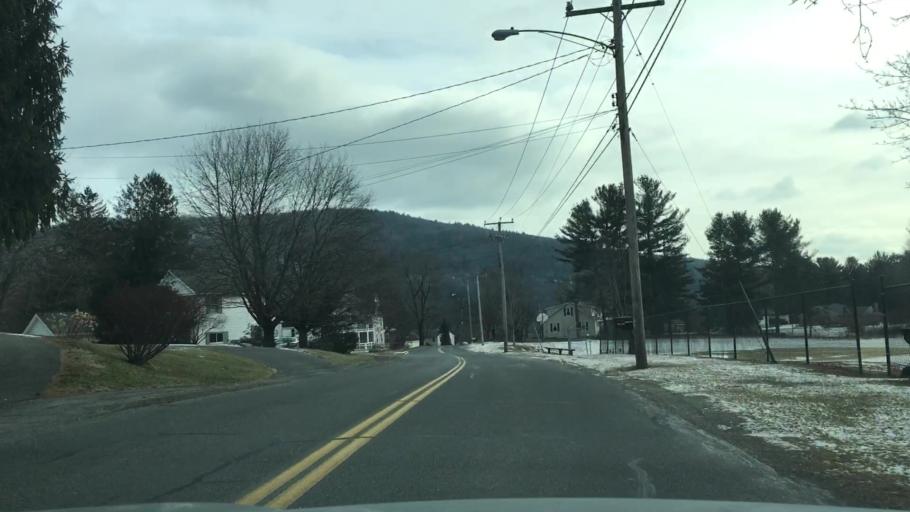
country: US
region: Massachusetts
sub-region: Berkshire County
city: Lee
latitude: 42.2933
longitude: -73.2460
